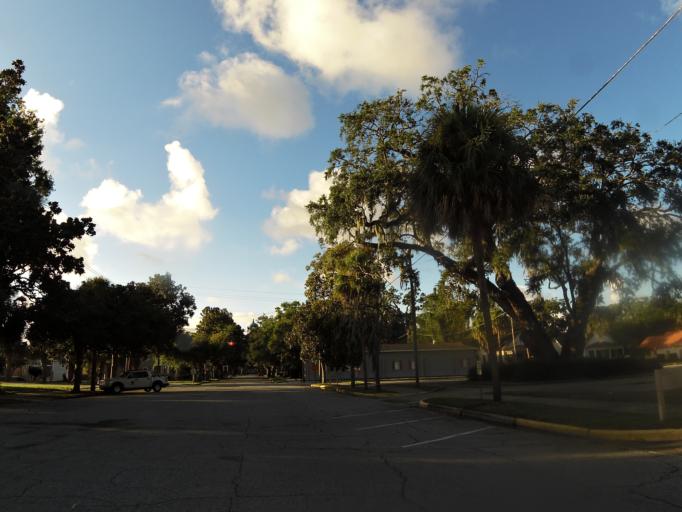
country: US
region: Georgia
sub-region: Glynn County
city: Brunswick
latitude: 31.1504
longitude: -81.4936
